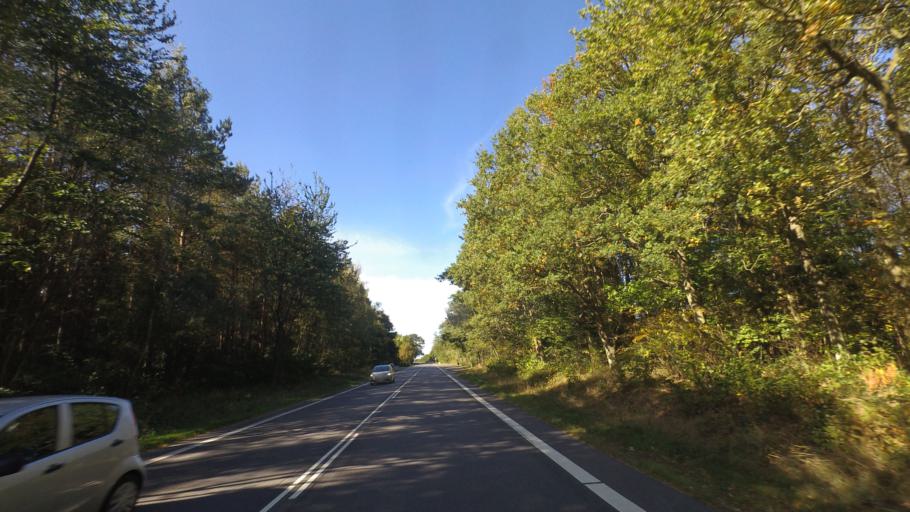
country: DK
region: Capital Region
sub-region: Bornholm Kommune
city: Ronne
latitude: 55.0834
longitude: 14.7504
